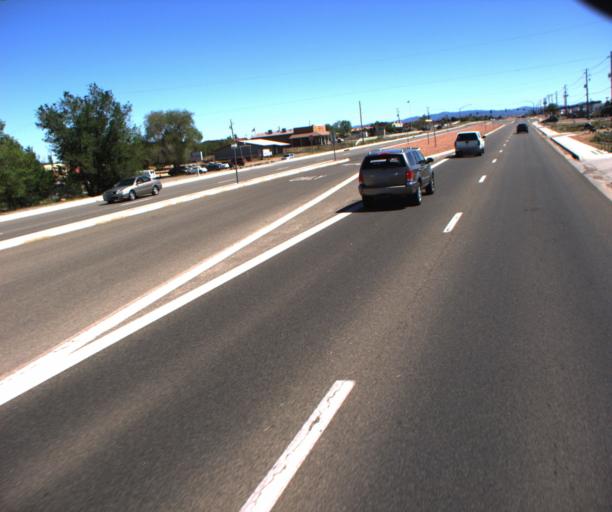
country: US
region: Arizona
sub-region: Yavapai County
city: Chino Valley
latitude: 34.7344
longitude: -112.4543
